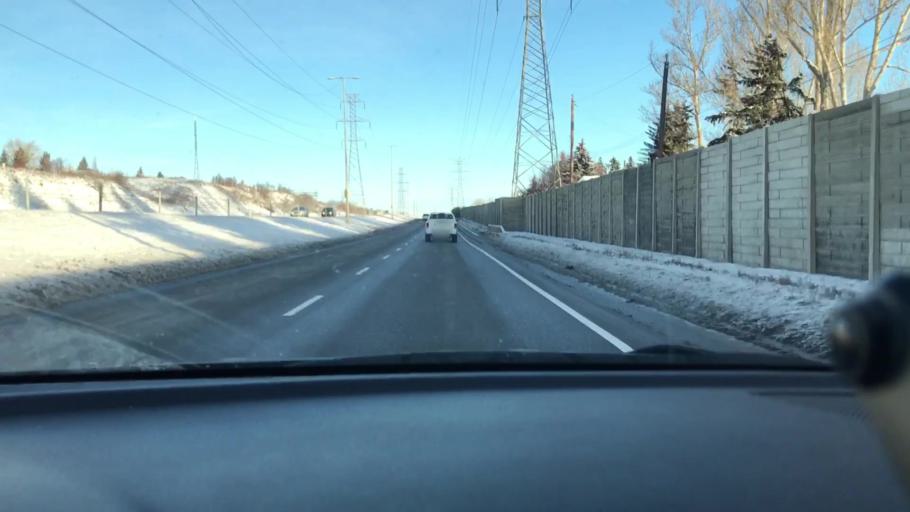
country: CA
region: Alberta
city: Calgary
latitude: 51.0452
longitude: -114.1642
